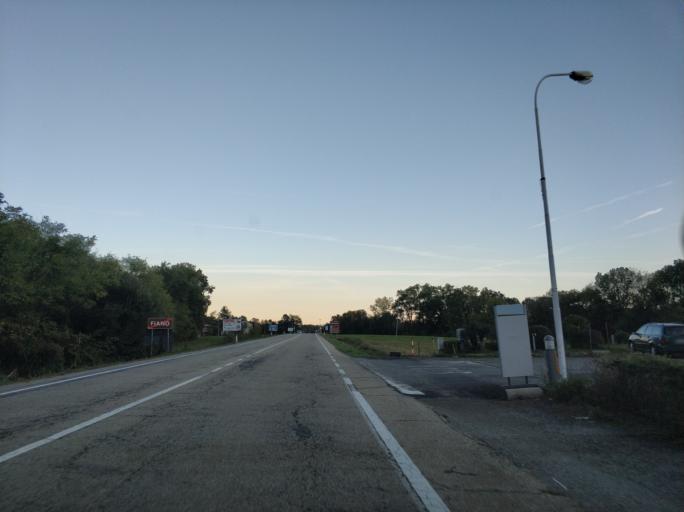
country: IT
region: Piedmont
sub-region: Provincia di Torino
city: Fiano
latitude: 45.2189
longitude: 7.5379
